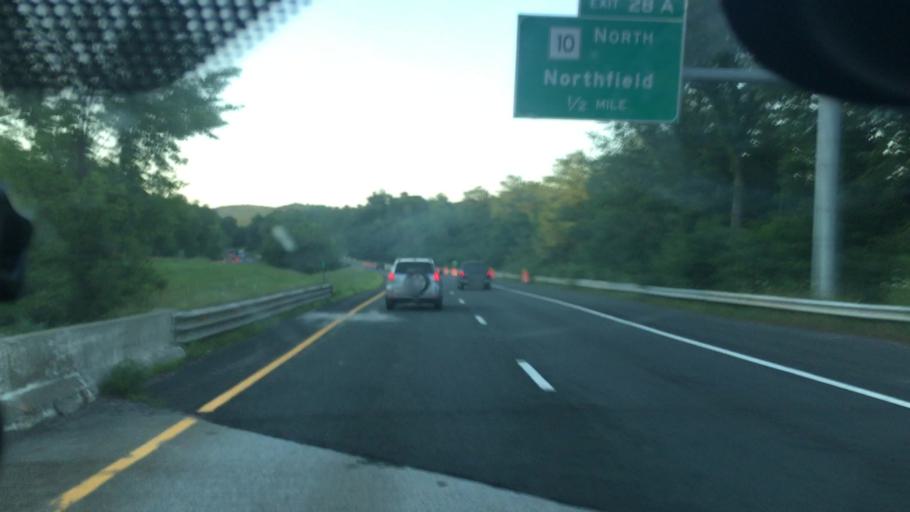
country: US
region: Massachusetts
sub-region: Franklin County
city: Bernardston
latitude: 42.6614
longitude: -72.5459
